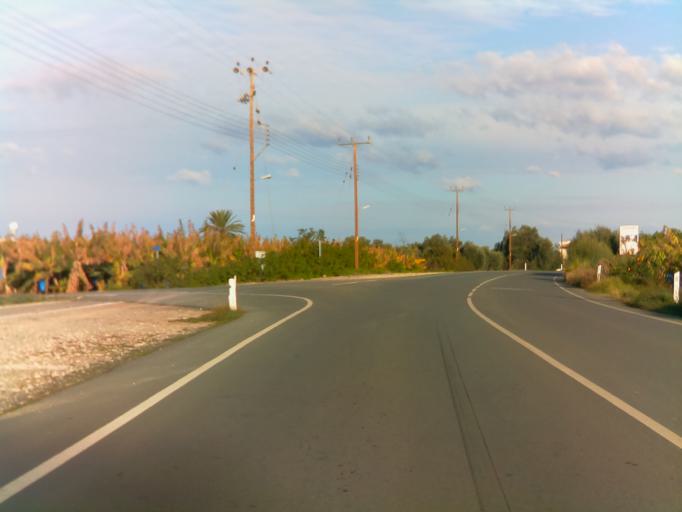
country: CY
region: Pafos
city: Pegeia
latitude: 34.8936
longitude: 32.3346
